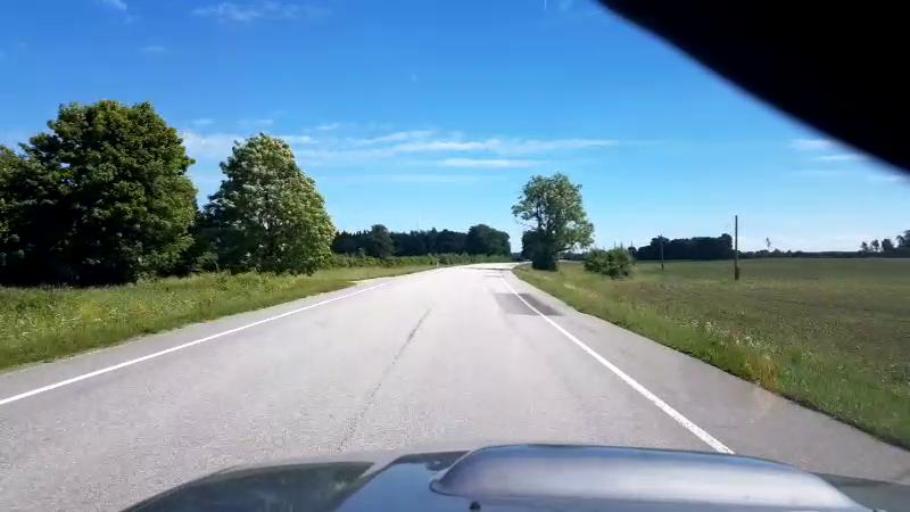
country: EE
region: Jaervamaa
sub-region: Koeru vald
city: Koeru
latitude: 58.9910
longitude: 25.9670
